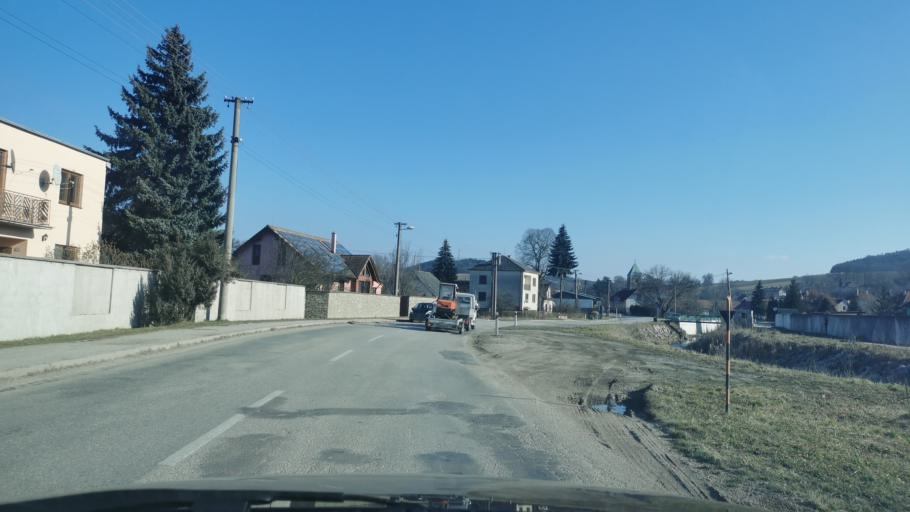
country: SK
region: Trenciansky
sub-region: Okres Myjava
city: Myjava
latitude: 48.7478
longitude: 17.5300
